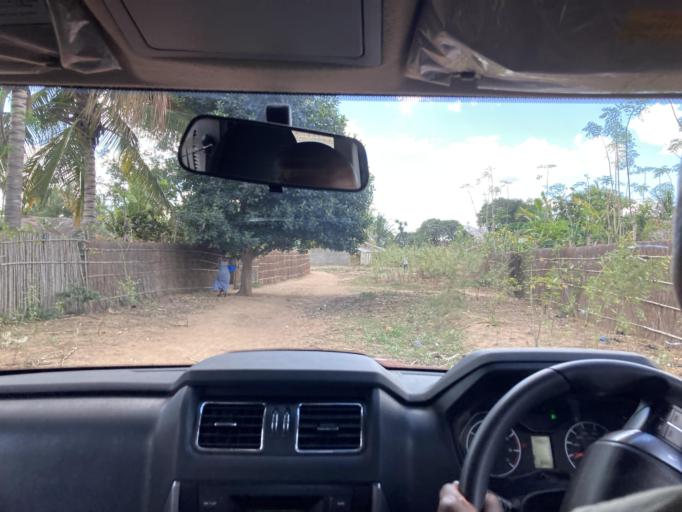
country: MZ
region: Cabo Delgado
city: Montepuez
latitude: -13.1465
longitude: 39.0002
